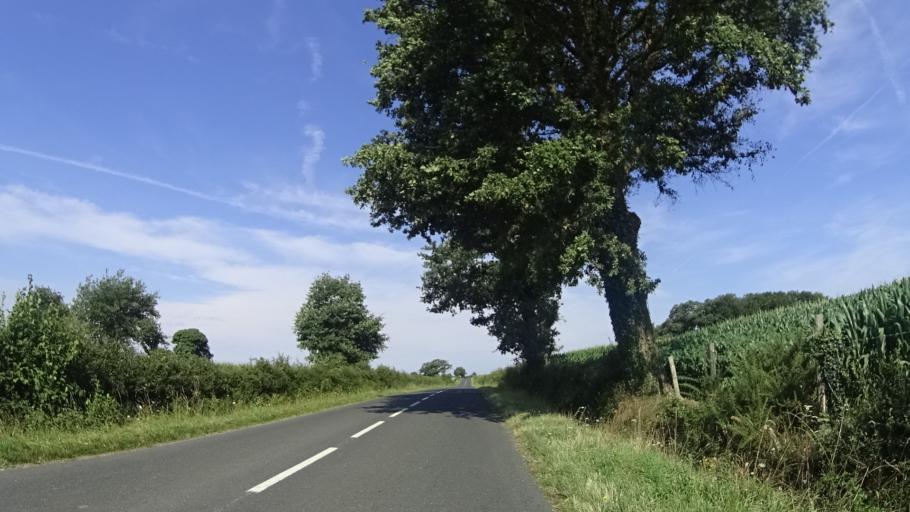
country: FR
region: Pays de la Loire
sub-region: Departement de la Loire-Atlantique
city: Joue-sur-Erdre
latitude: 47.5013
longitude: -1.4621
